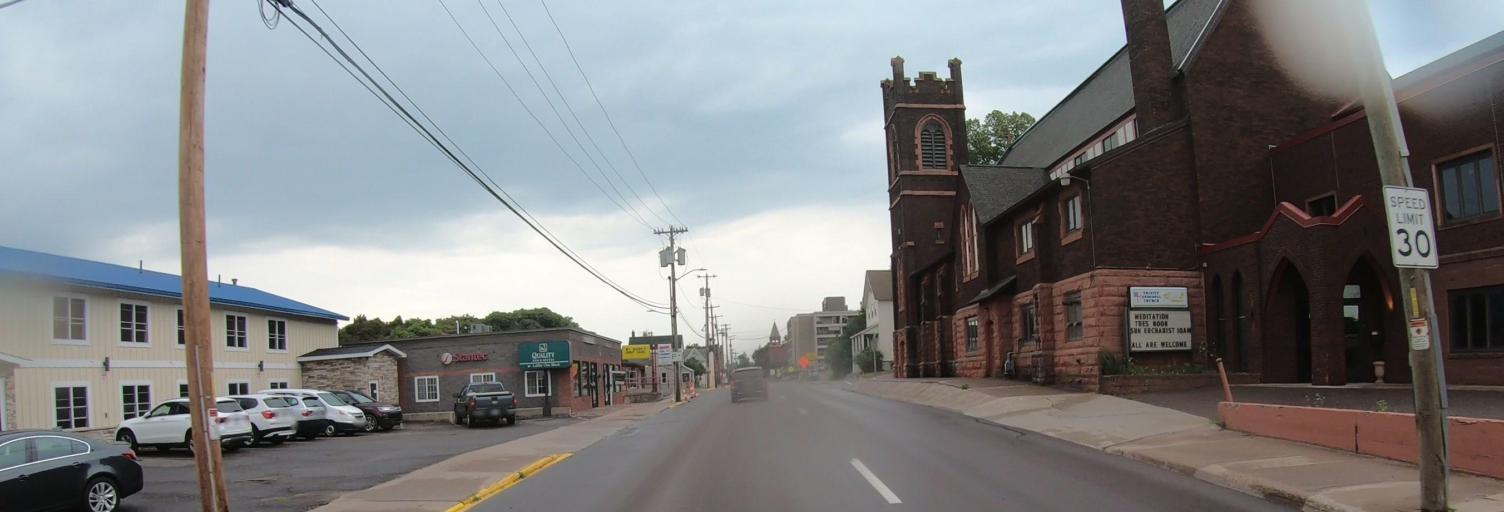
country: US
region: Michigan
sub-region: Houghton County
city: Houghton
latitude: 47.1211
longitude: -88.5714
